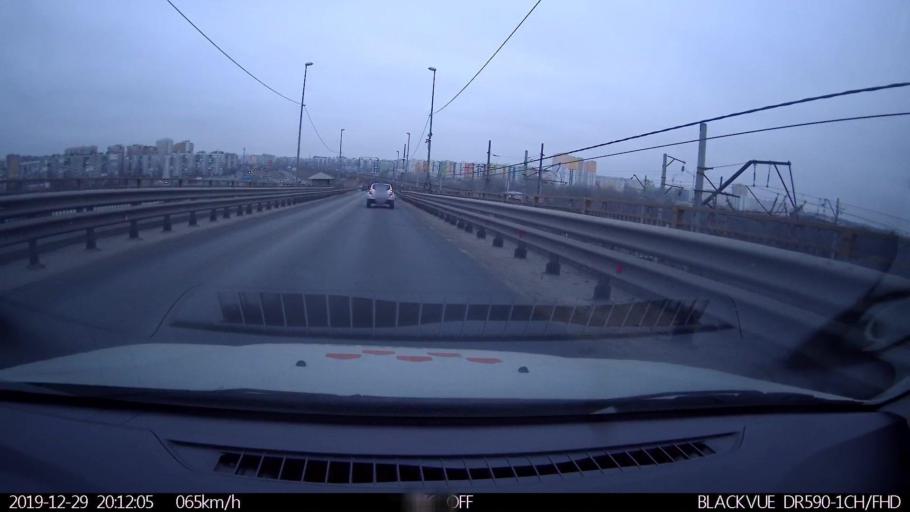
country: RU
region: Nizjnij Novgorod
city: Nizhniy Novgorod
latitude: 56.3498
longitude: 43.9222
